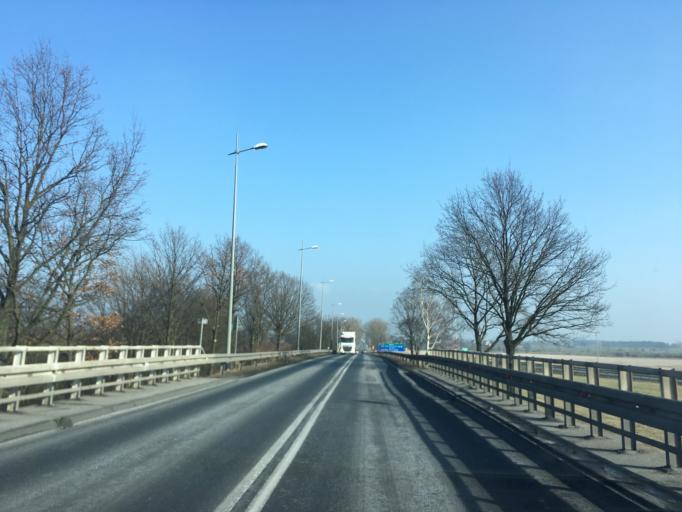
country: PL
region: Lower Silesian Voivodeship
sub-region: Powiat zlotoryjski
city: Olszanica
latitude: 51.2740
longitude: 15.7941
